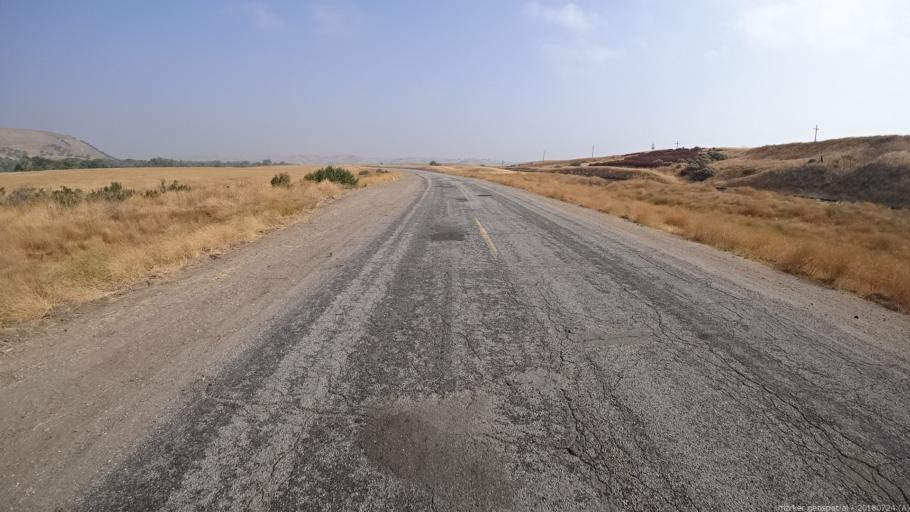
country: US
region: California
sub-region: San Luis Obispo County
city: San Miguel
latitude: 35.8281
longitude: -120.7503
